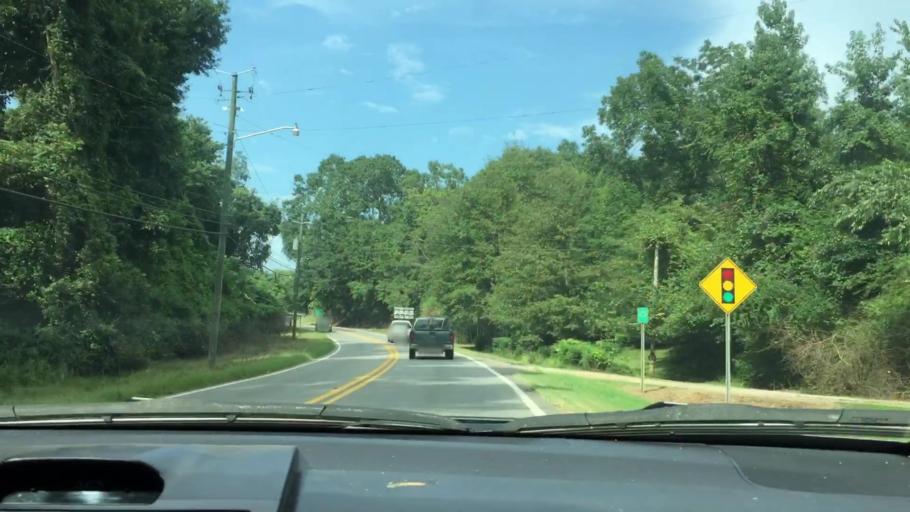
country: US
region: Alabama
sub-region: Hale County
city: Greensboro
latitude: 32.6982
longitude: -87.6014
